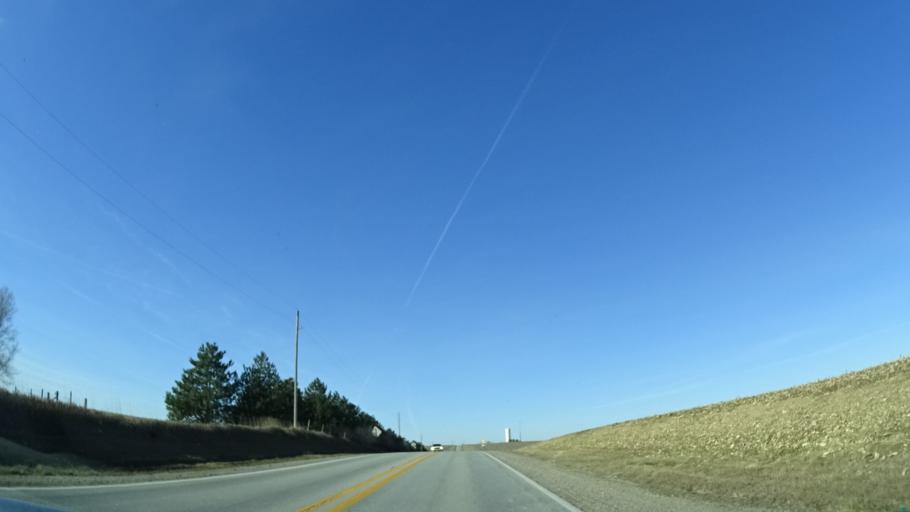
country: US
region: Nebraska
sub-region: Sarpy County
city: Springfield
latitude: 41.0889
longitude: -96.1014
